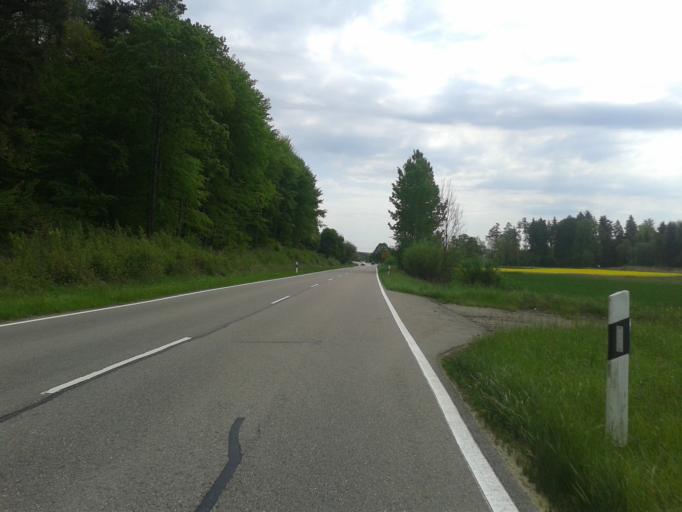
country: DE
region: Baden-Wuerttemberg
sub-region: Tuebingen Region
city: Erbach
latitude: 48.3543
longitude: 9.8540
